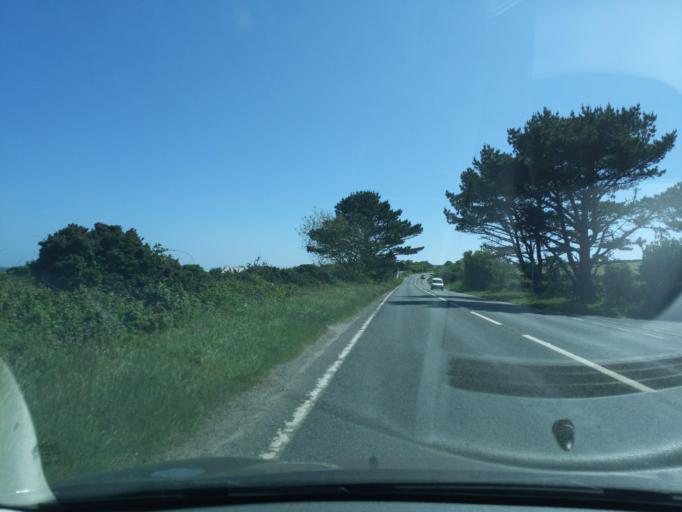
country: GB
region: England
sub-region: Cornwall
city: Wendron
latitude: 50.1377
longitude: -5.2200
